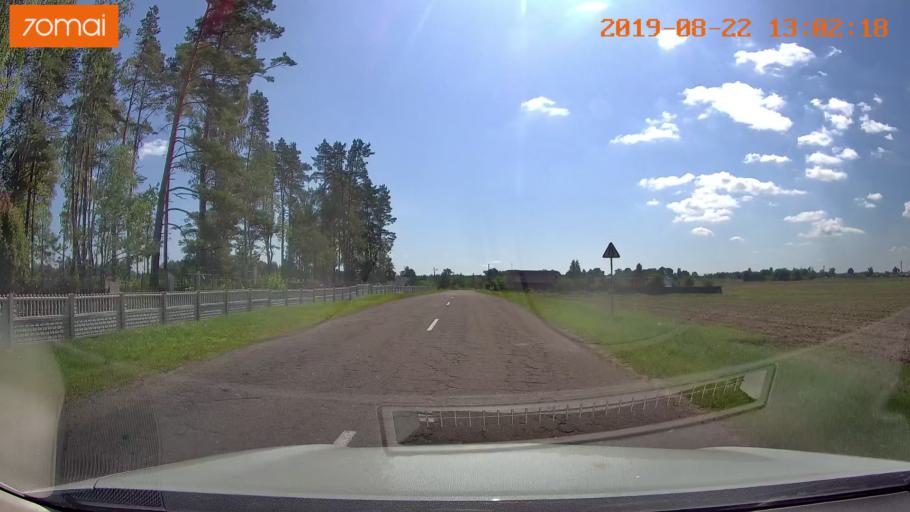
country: BY
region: Minsk
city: Prawdzinski
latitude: 53.3904
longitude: 27.8246
